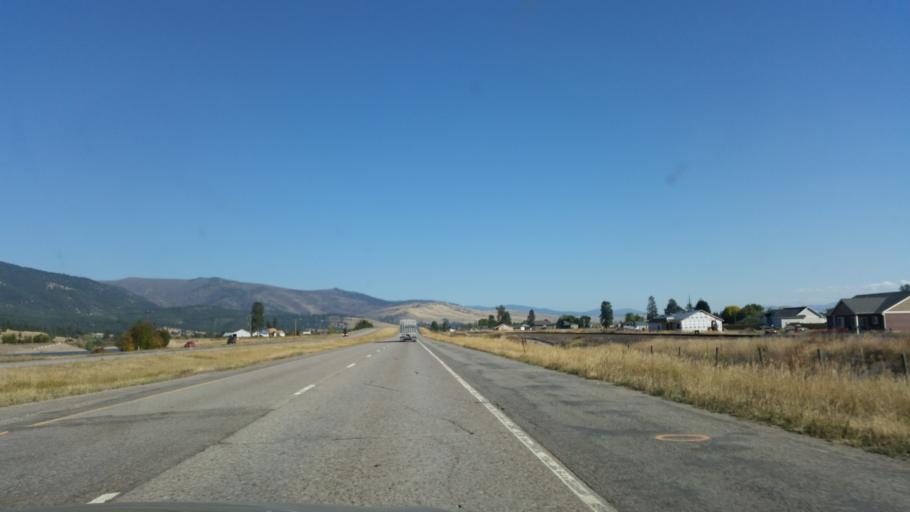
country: US
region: Montana
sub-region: Missoula County
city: Frenchtown
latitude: 47.0285
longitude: -114.3028
